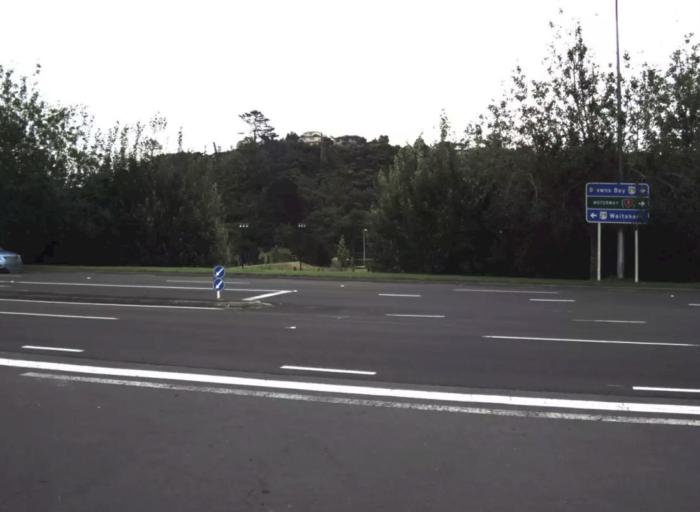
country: NZ
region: Auckland
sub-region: Auckland
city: Rothesay Bay
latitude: -36.7245
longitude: 174.7012
